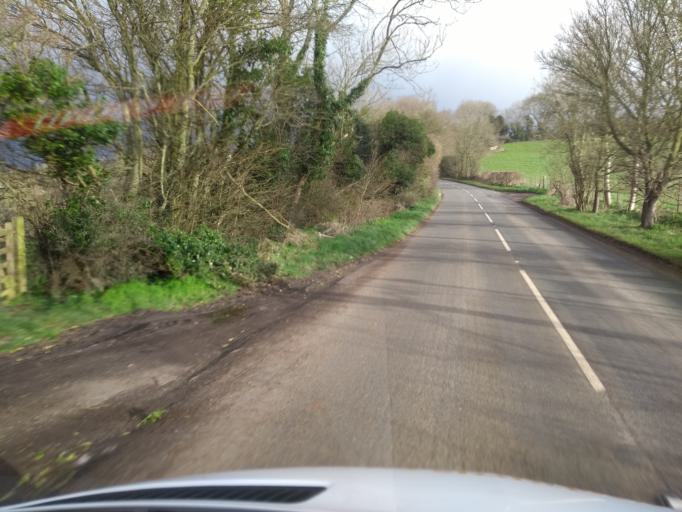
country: GB
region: England
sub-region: Somerset
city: Bruton
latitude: 51.0943
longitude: -2.4655
